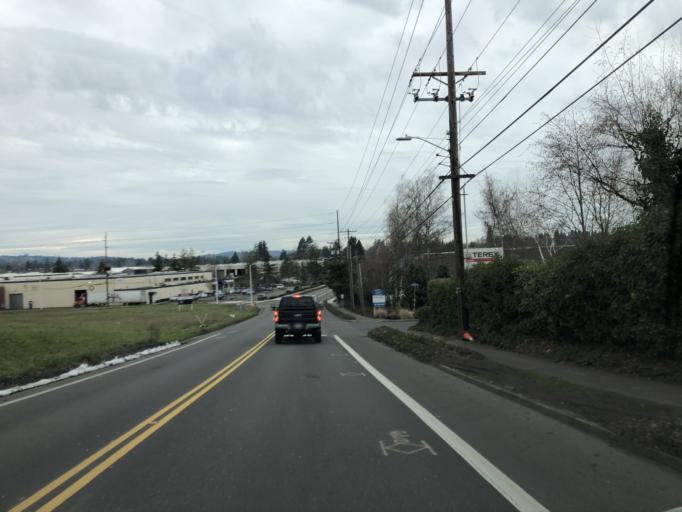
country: US
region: Oregon
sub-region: Washington County
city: Tigard
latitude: 45.4271
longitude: -122.7561
